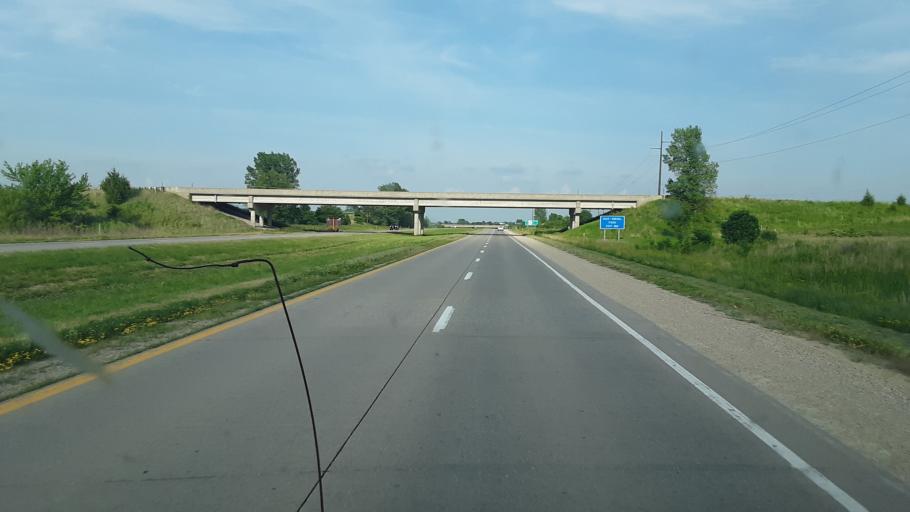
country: US
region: Iowa
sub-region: Marshall County
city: Marshalltown
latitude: 42.0031
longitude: -92.8948
